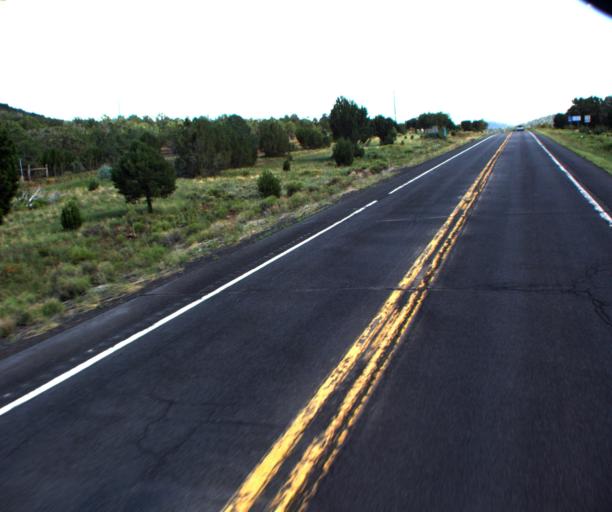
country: US
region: Arizona
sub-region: Coconino County
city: Williams
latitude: 35.3499
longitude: -112.1668
